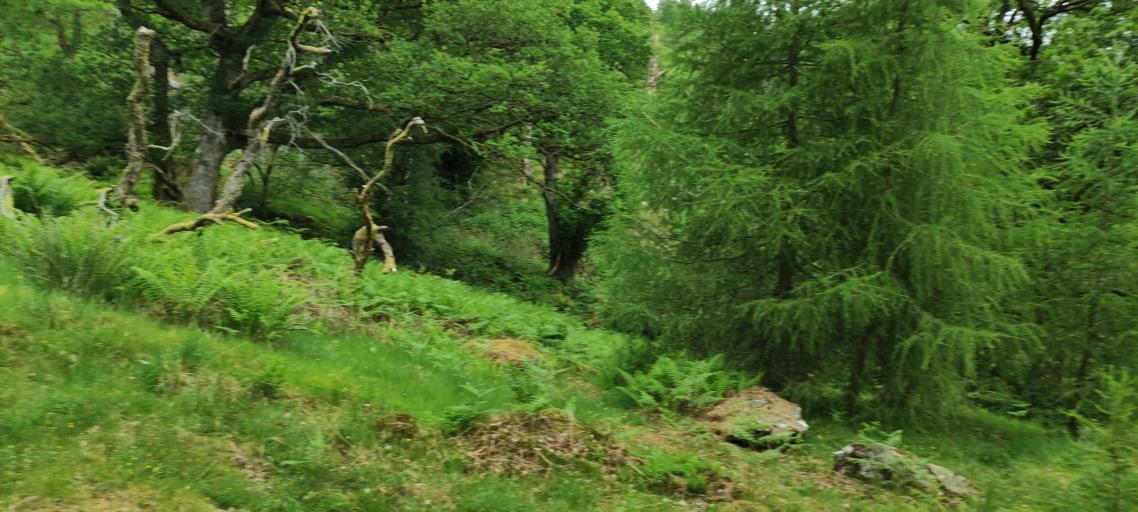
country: GB
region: England
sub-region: Cumbria
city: Ambleside
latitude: 54.5520
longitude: -2.9542
